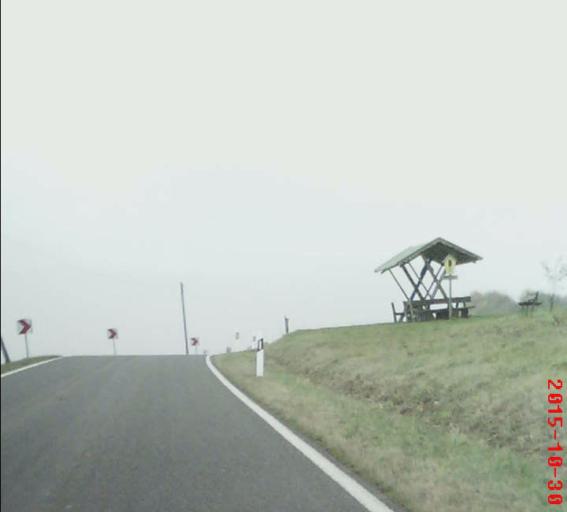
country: DE
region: Thuringia
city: Wachstedt
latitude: 51.2979
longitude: 10.2366
